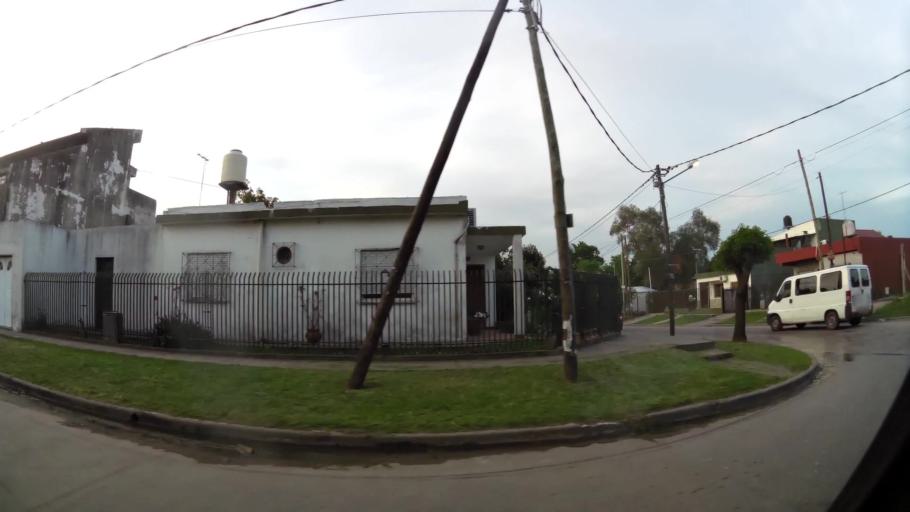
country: AR
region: Buenos Aires
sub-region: Partido de Quilmes
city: Quilmes
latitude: -34.7995
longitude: -58.2881
